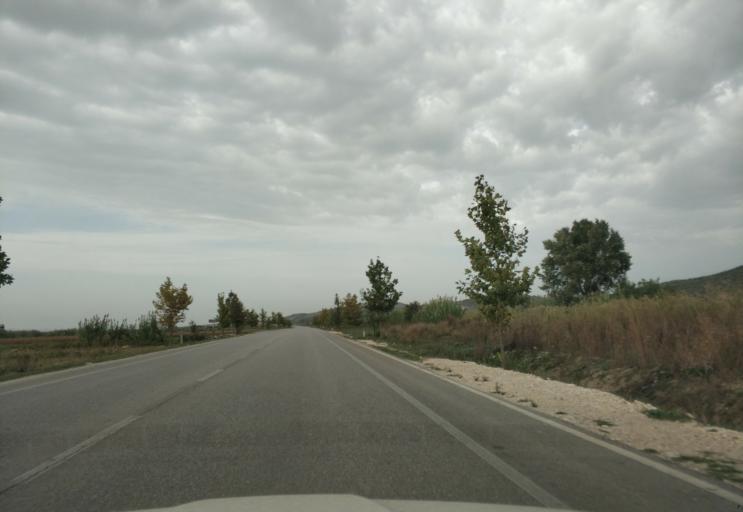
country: AL
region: Fier
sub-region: Rrethi i Fierit
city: Levan
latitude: 40.6621
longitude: 19.4889
